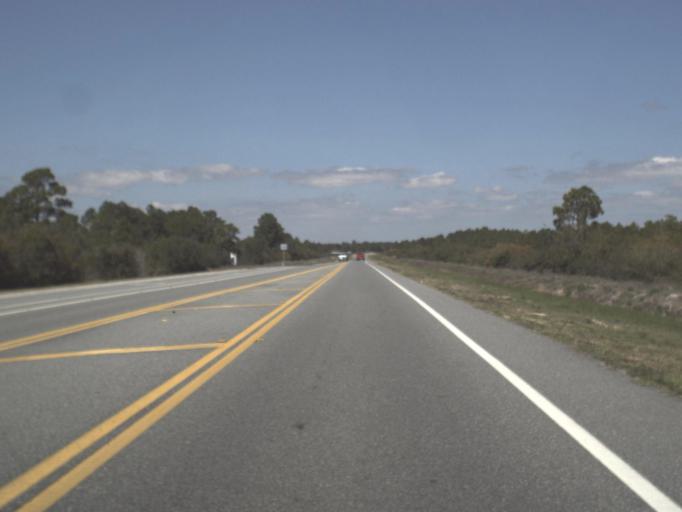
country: US
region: Florida
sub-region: Gulf County
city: Port Saint Joe
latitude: 29.8629
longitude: -85.3372
